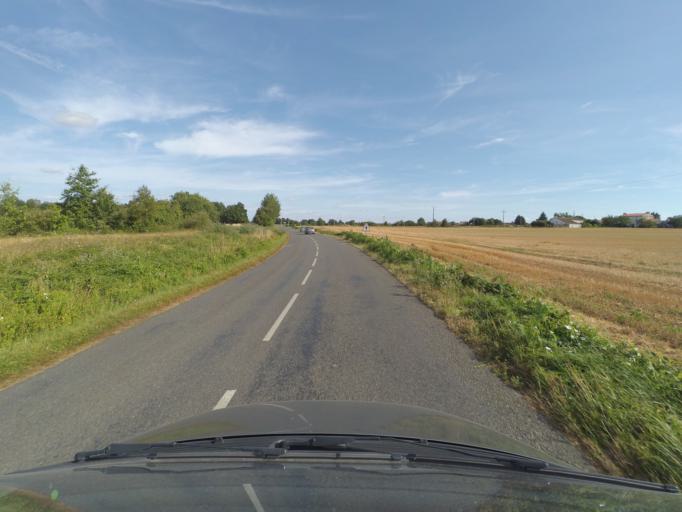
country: FR
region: Pays de la Loire
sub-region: Departement de la Loire-Atlantique
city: Montbert
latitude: 47.0292
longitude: -1.4687
